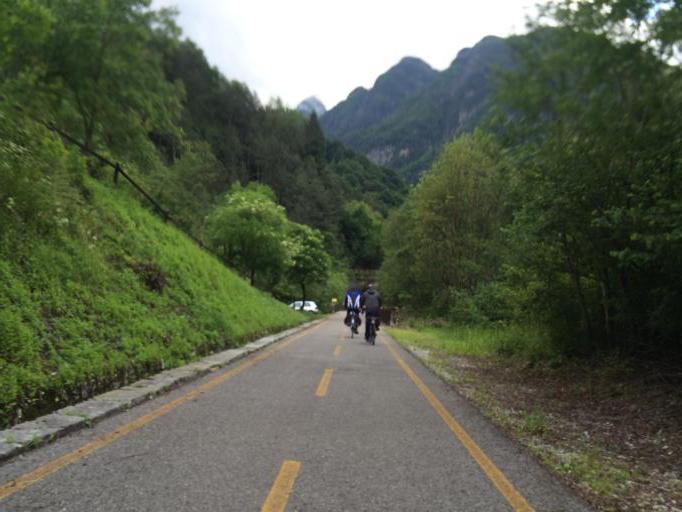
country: IT
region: Friuli Venezia Giulia
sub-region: Provincia di Udine
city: Dogna
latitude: 46.4541
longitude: 13.3149
